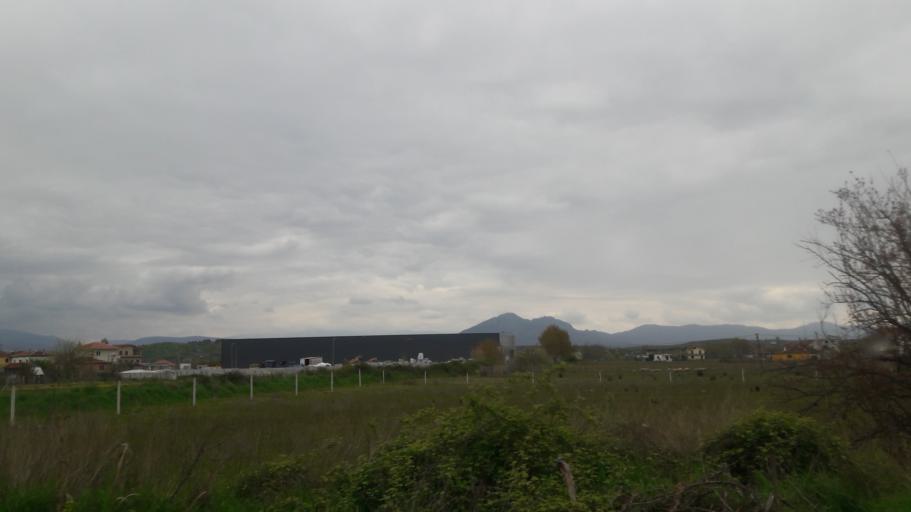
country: AL
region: Shkoder
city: Vukatane
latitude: 41.9703
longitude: 19.5397
